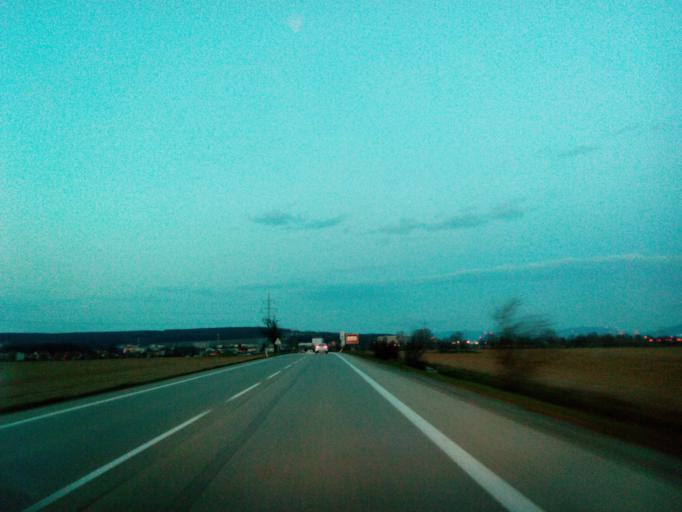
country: SK
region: Kosicky
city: Kosice
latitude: 48.6244
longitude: 21.1559
